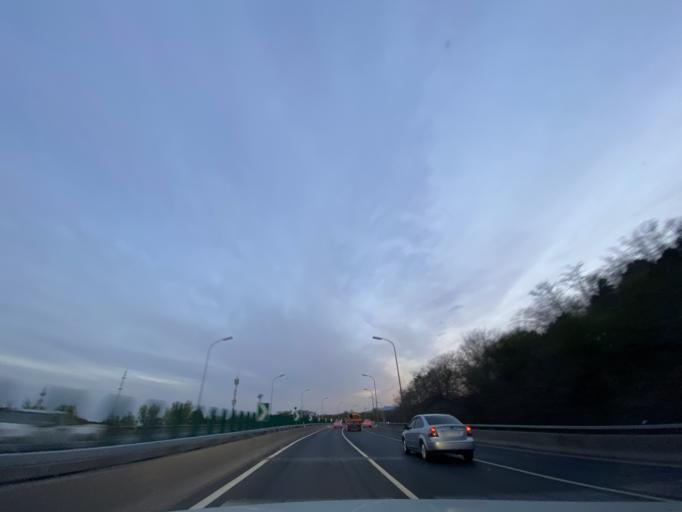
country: CN
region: Beijing
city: Haidian
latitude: 40.0050
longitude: 116.2640
